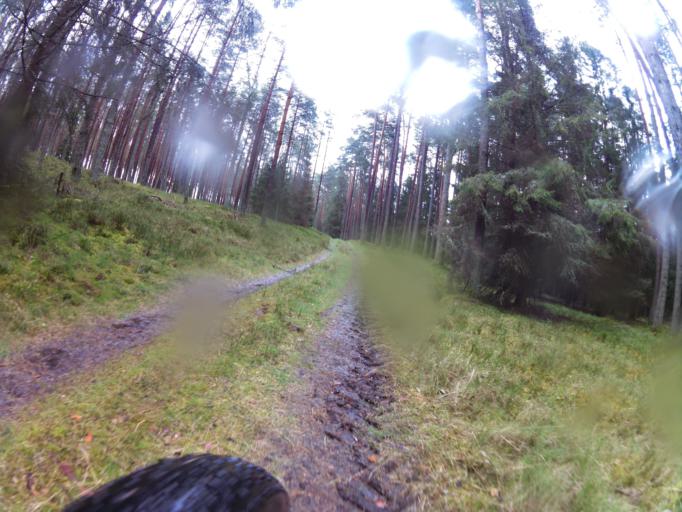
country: PL
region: Pomeranian Voivodeship
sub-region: Powiat slupski
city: Kepice
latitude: 54.2401
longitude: 16.7779
